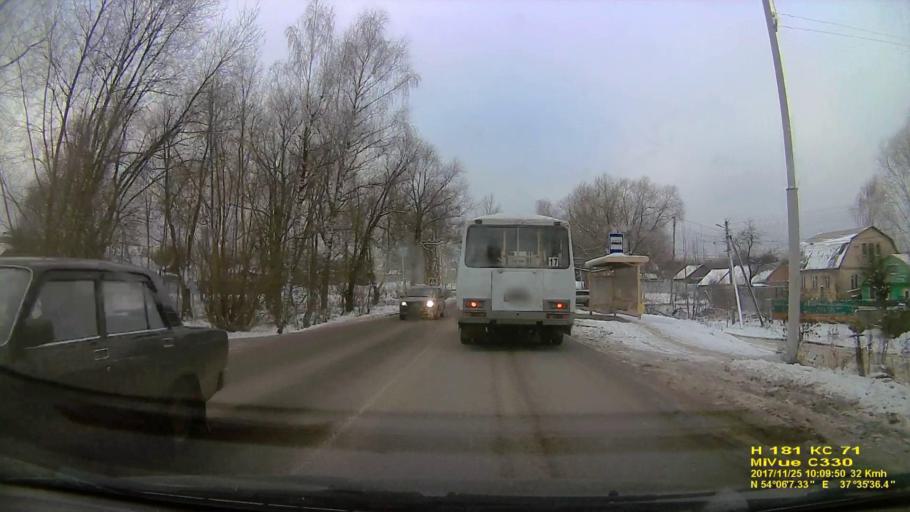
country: RU
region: Tula
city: Skuratovskiy
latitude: 54.1020
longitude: 37.5934
